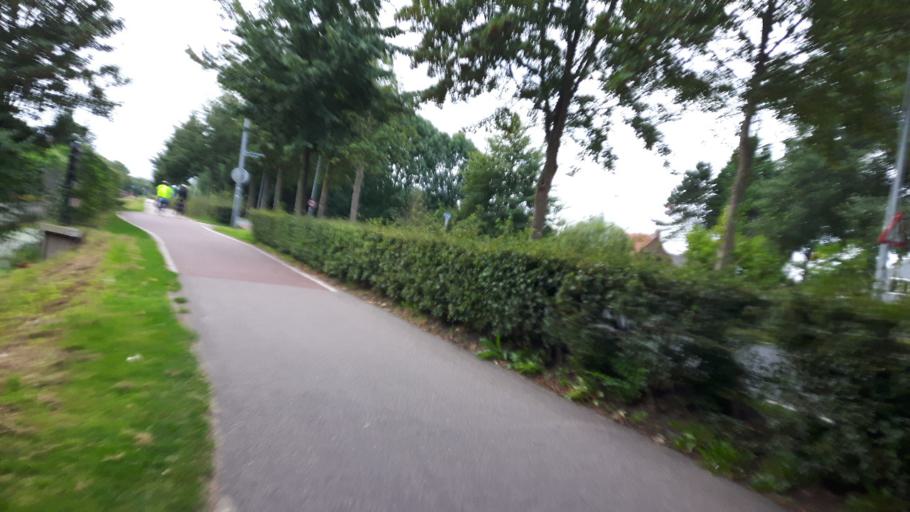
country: NL
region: North Holland
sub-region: Gemeente Hoorn
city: Hoorn
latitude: 52.6626
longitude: 5.0414
